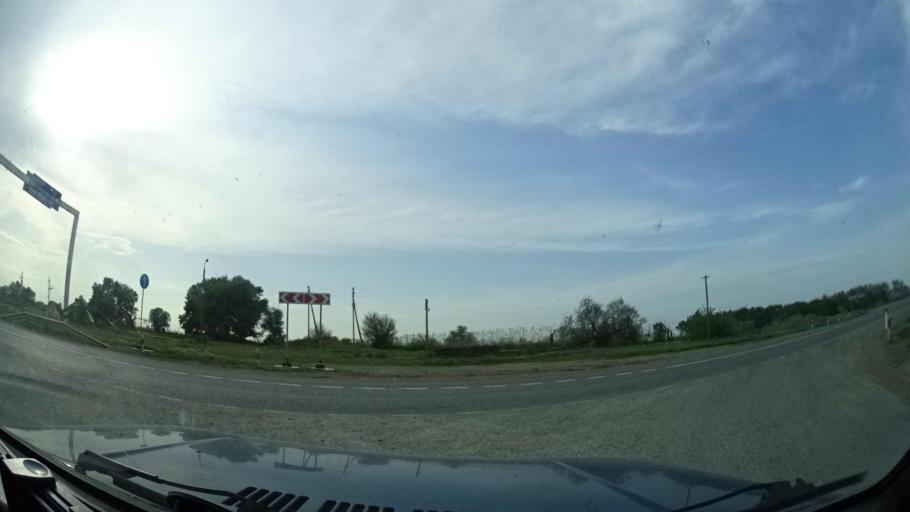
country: RU
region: Dagestan
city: Babayurt
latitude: 43.5753
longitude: 46.7380
